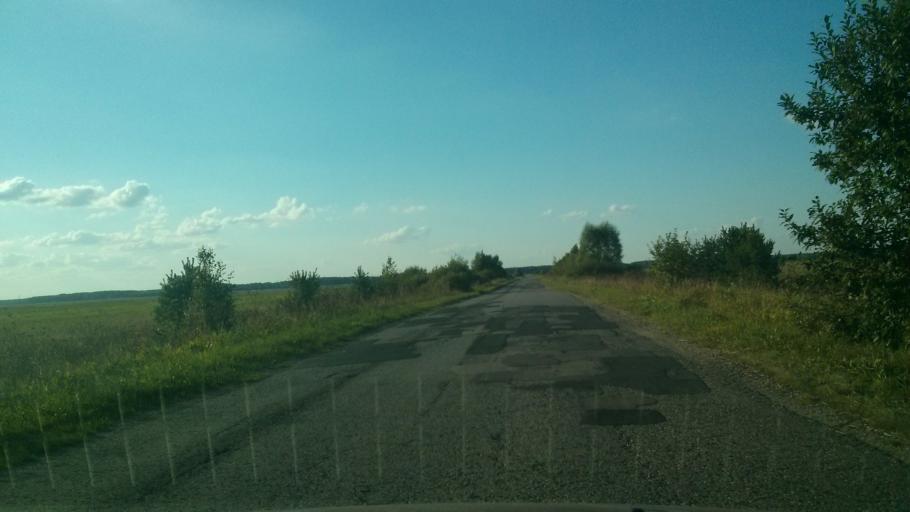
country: RU
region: Vladimir
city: Melenki
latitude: 55.3007
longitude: 41.7915
